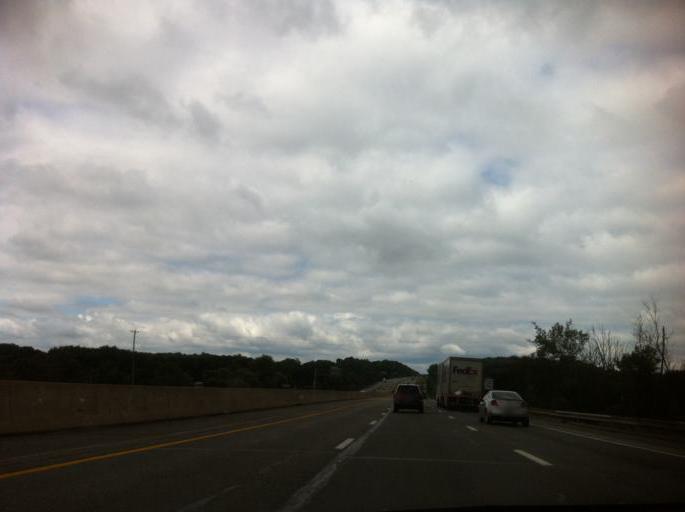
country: US
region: Ohio
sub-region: Portage County
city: Mantua
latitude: 41.2458
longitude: -81.2487
